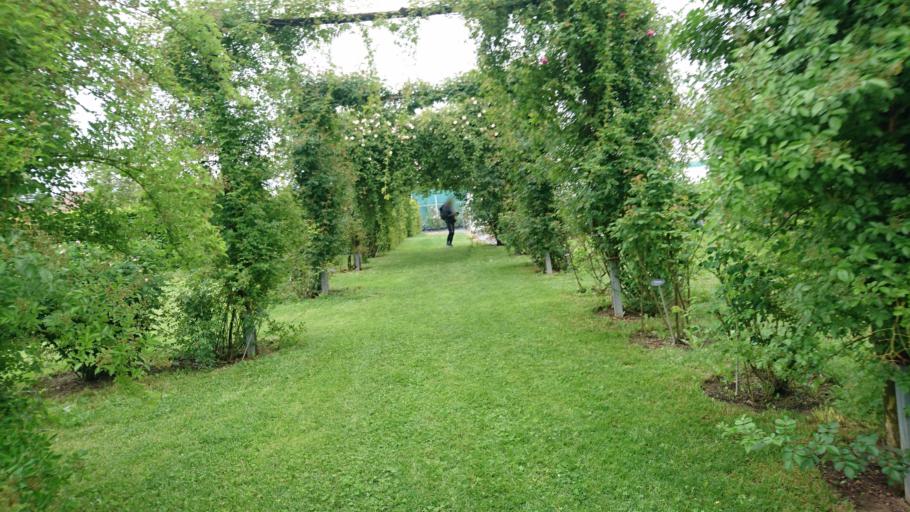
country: IT
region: Veneto
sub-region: Provincia di Vicenza
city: Montegaldella
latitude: 45.4145
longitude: 11.6627
